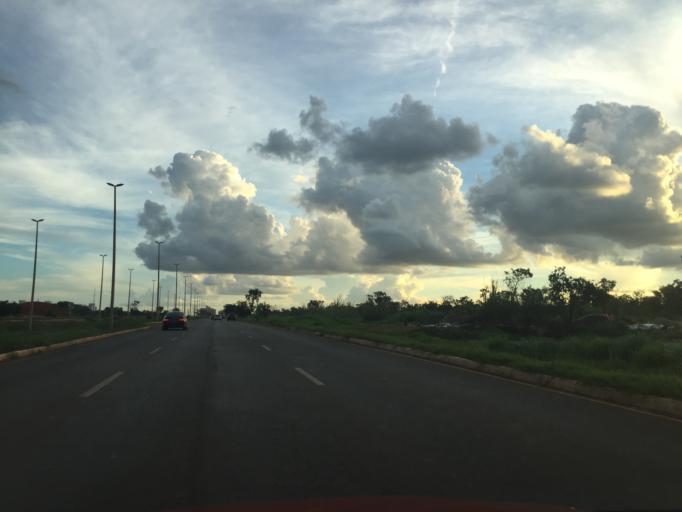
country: BR
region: Federal District
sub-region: Brasilia
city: Brasilia
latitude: -15.8020
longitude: -47.9917
